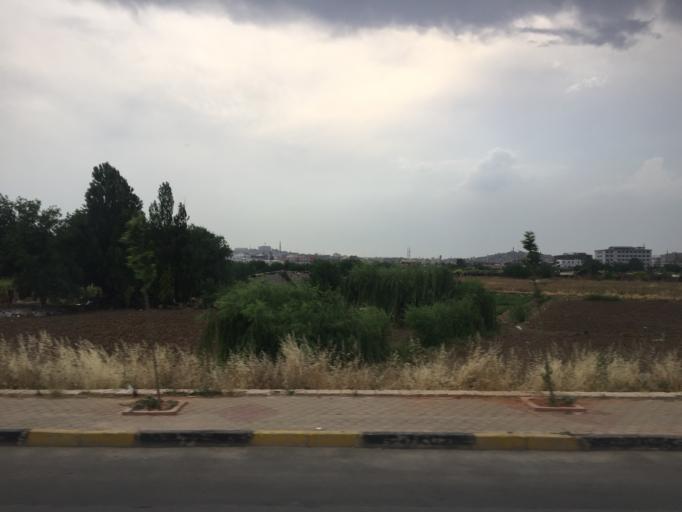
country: TR
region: Gaziantep
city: Gaziantep
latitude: 37.0586
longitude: 37.4157
